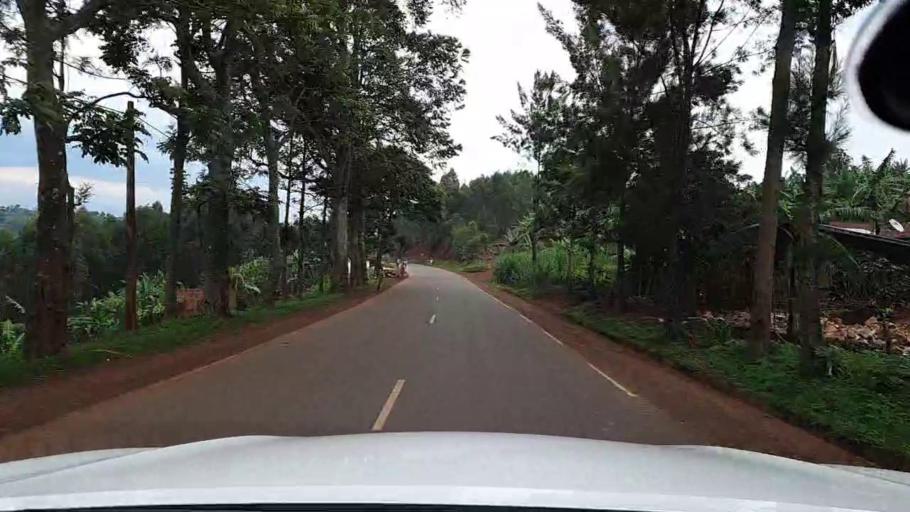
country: RW
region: Western Province
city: Cyangugu
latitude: -2.6120
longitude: 28.9382
